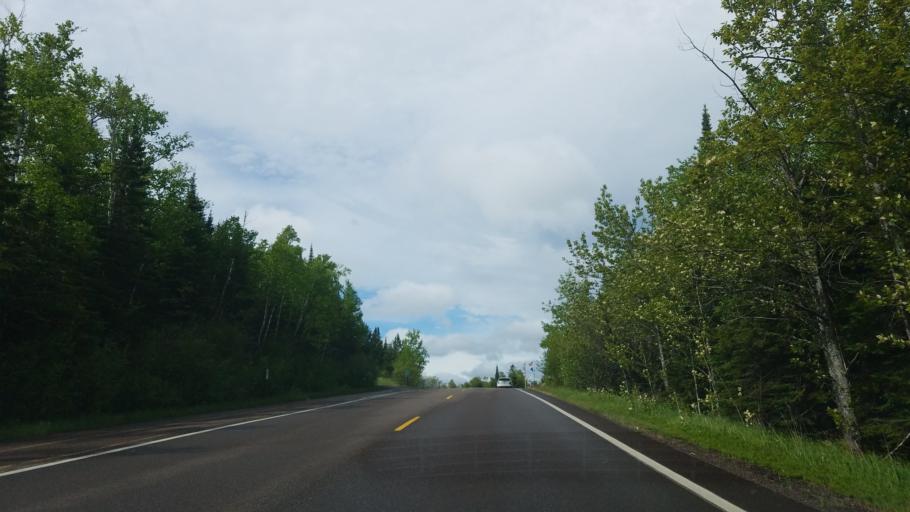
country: US
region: Minnesota
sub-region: Lake County
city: Silver Bay
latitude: 47.2040
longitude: -91.3684
